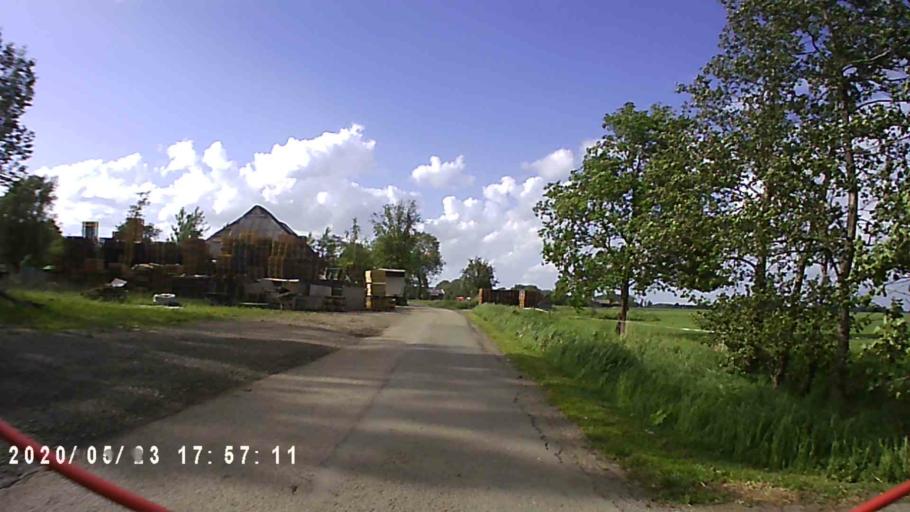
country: NL
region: Groningen
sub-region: Gemeente Slochteren
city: Slochteren
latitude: 53.2514
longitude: 6.7418
